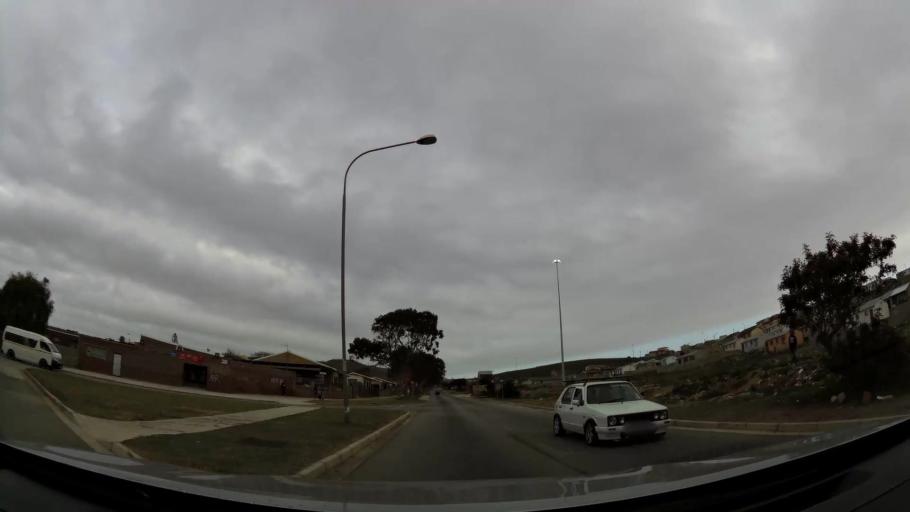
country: ZA
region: Eastern Cape
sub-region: Nelson Mandela Bay Metropolitan Municipality
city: Port Elizabeth
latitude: -33.9116
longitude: 25.5468
